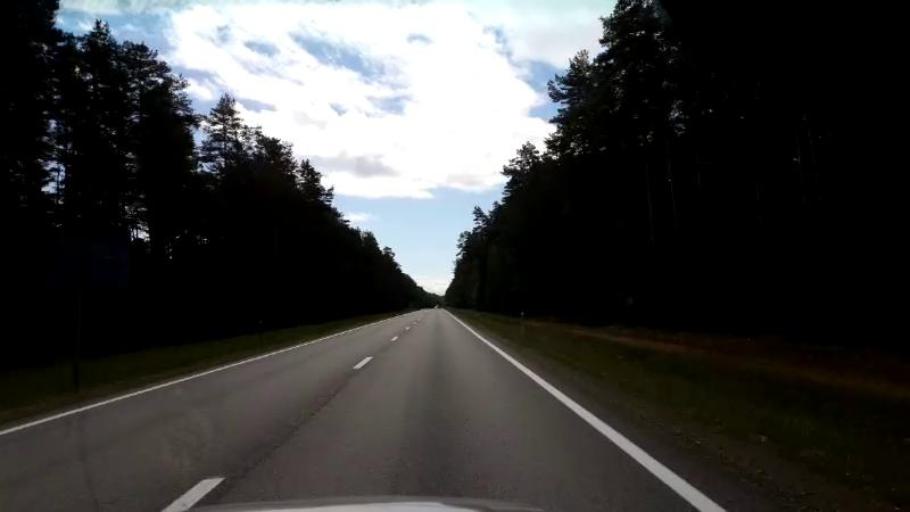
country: LV
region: Salacgrivas
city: Salacgriva
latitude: 57.5132
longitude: 24.4306
